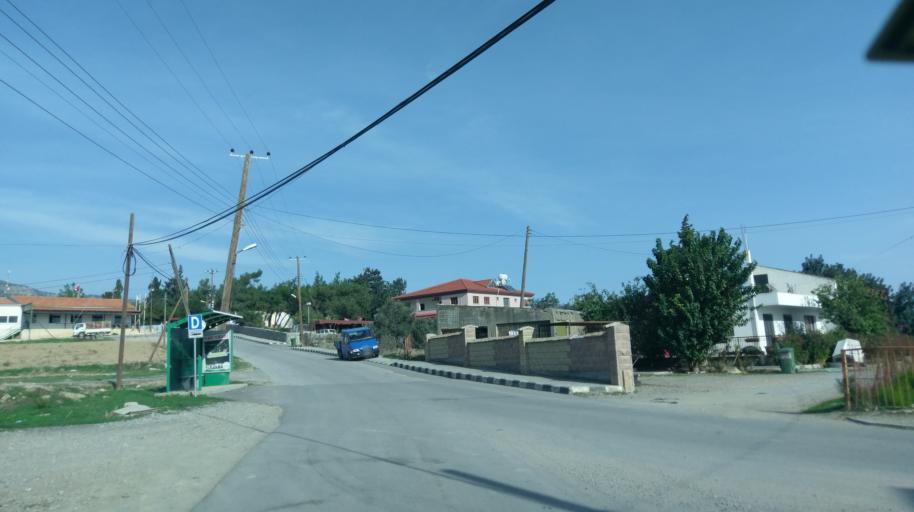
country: CY
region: Keryneia
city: Lapithos
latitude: 35.2653
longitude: 33.2232
